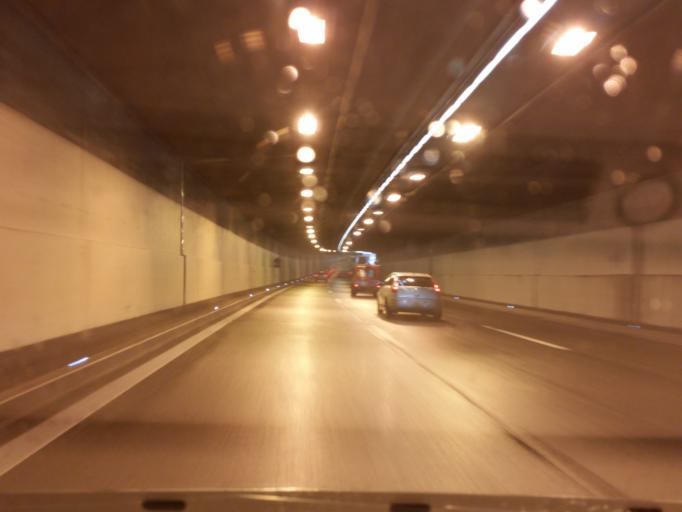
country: CH
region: Zurich
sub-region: Bezirk Buelach
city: Glattbrugg / Wydacker/Bettacker/Laettenwiesen
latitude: 47.4252
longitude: 8.5633
